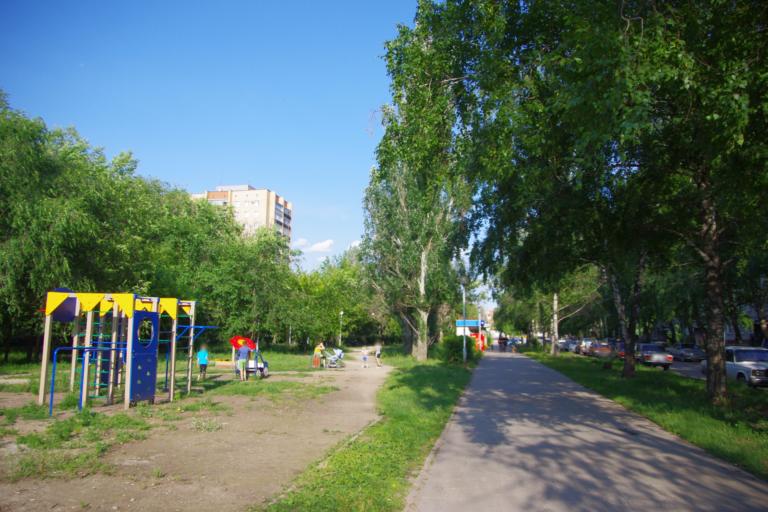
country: RU
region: Samara
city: Tol'yatti
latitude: 53.5086
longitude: 49.2869
